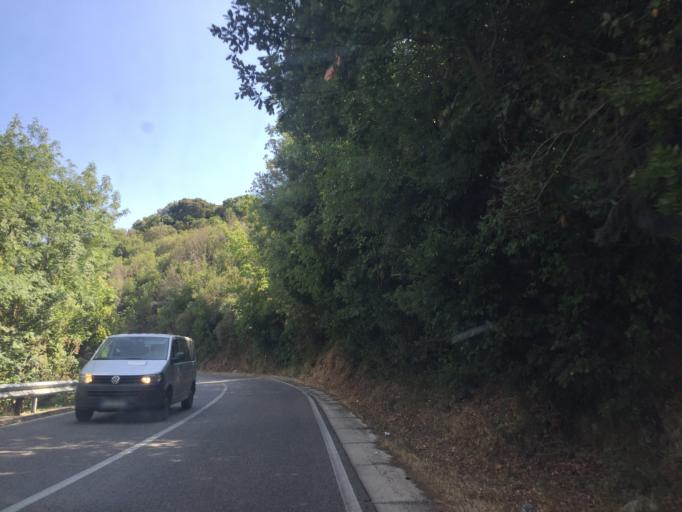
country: IT
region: Sardinia
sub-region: Provincia di Olbia-Tempio
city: Aggius
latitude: 40.9248
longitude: 9.0635
